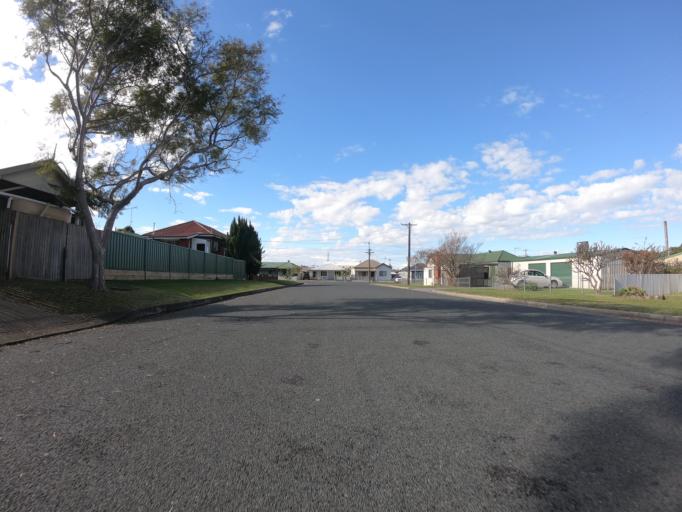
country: AU
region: New South Wales
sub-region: Wollongong
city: Corrimal
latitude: -34.3724
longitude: 150.9040
